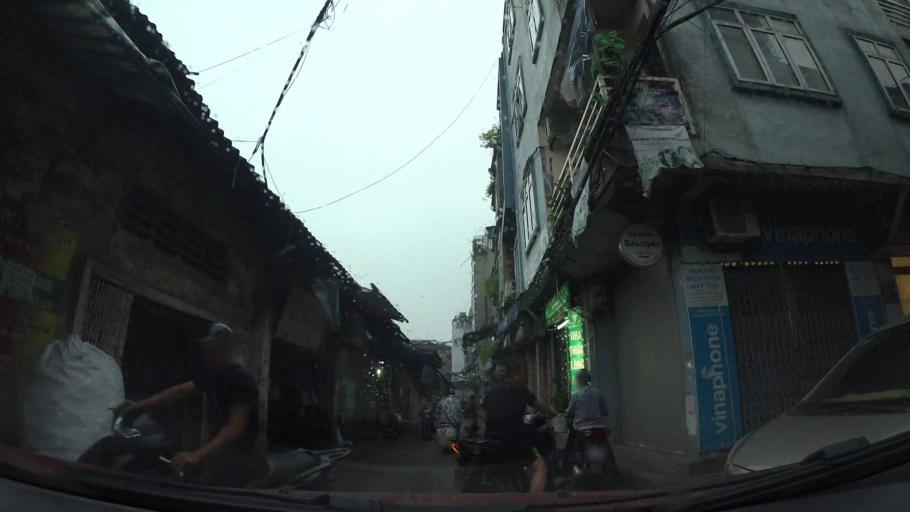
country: VN
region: Ha Noi
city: Hanoi
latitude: 21.0240
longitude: 105.8396
